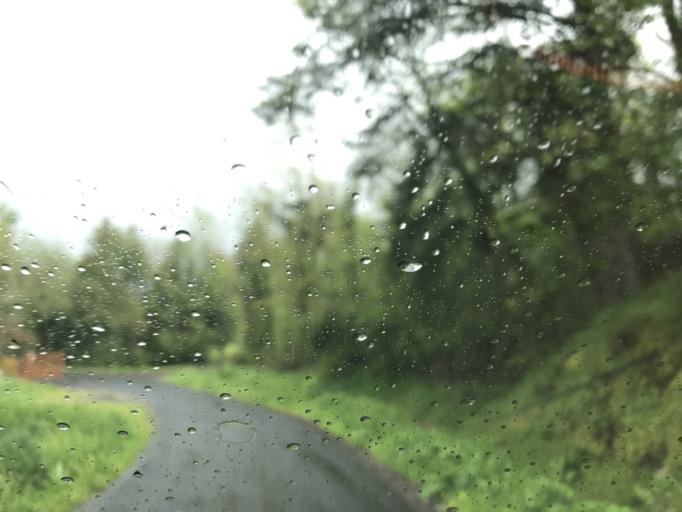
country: FR
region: Auvergne
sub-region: Departement du Puy-de-Dome
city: Courpiere
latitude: 45.7496
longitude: 3.5289
